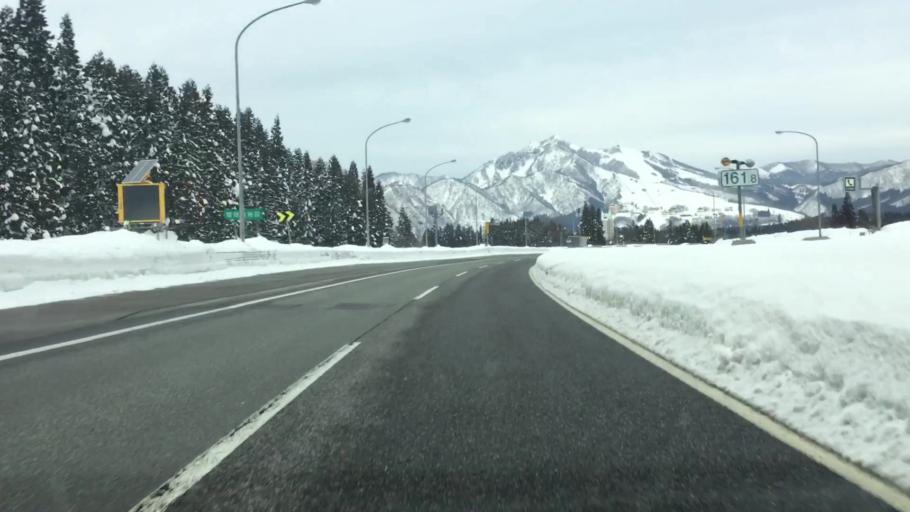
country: JP
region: Niigata
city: Shiozawa
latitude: 36.8942
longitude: 138.8454
